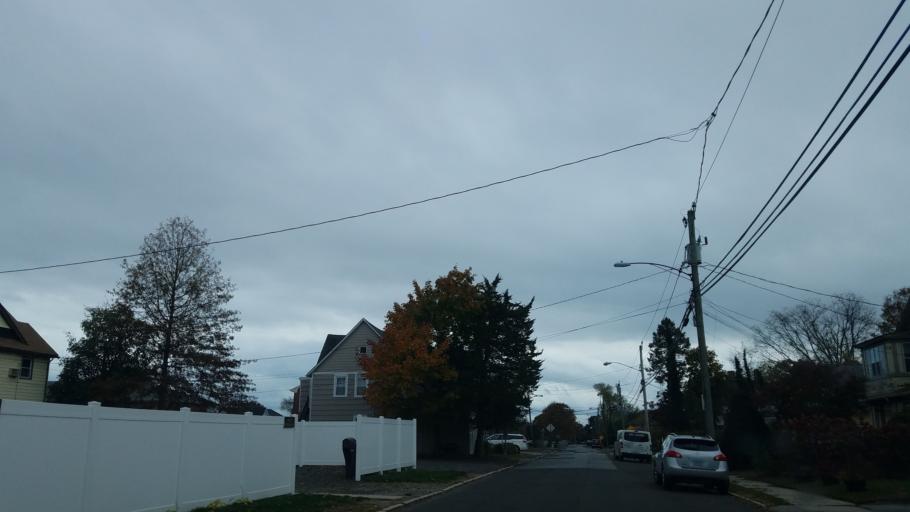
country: US
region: Connecticut
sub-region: Fairfield County
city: Stamford
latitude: 41.0585
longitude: -73.5078
